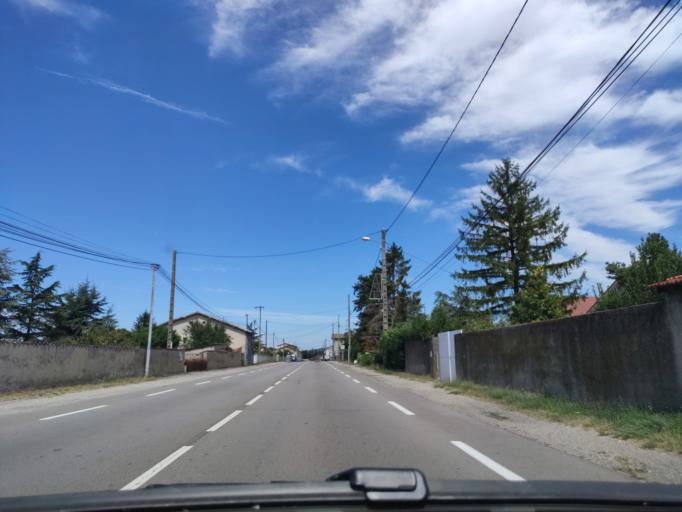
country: FR
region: Rhone-Alpes
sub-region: Departement de l'Isere
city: Auberives-sur-Vareze
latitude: 45.4192
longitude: 4.8164
